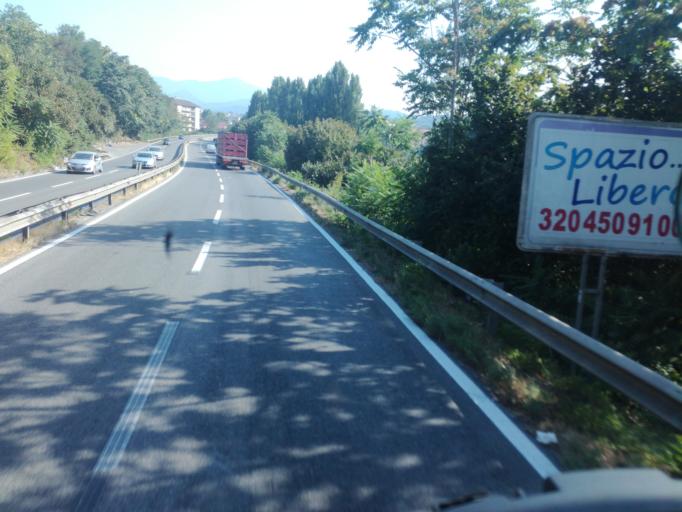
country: IT
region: Campania
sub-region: Provincia di Avellino
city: Atripalda
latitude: 40.9224
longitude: 14.8257
